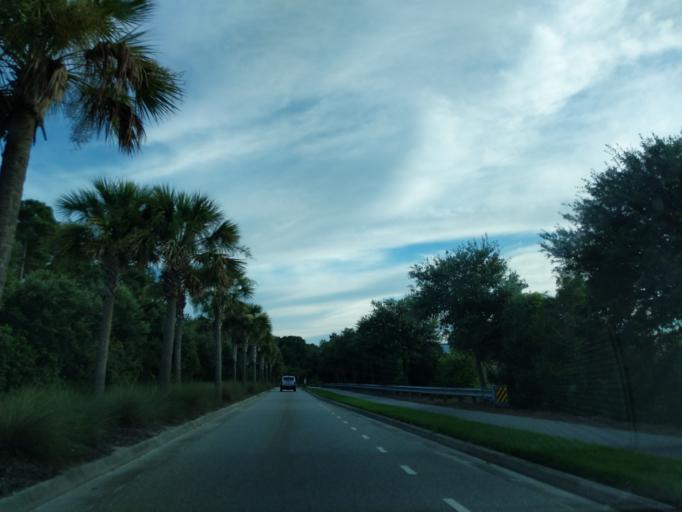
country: US
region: South Carolina
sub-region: Charleston County
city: Isle of Palms
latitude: 32.8362
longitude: -79.8172
